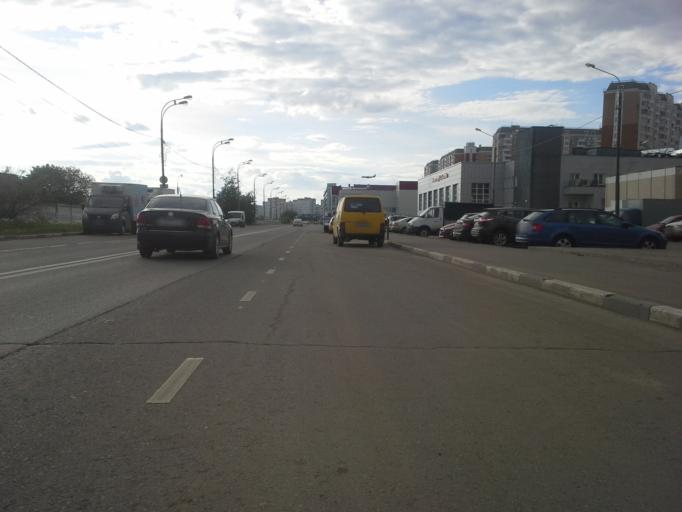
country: RU
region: Moskovskaya
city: Moskovskiy
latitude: 55.5889
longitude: 37.3696
